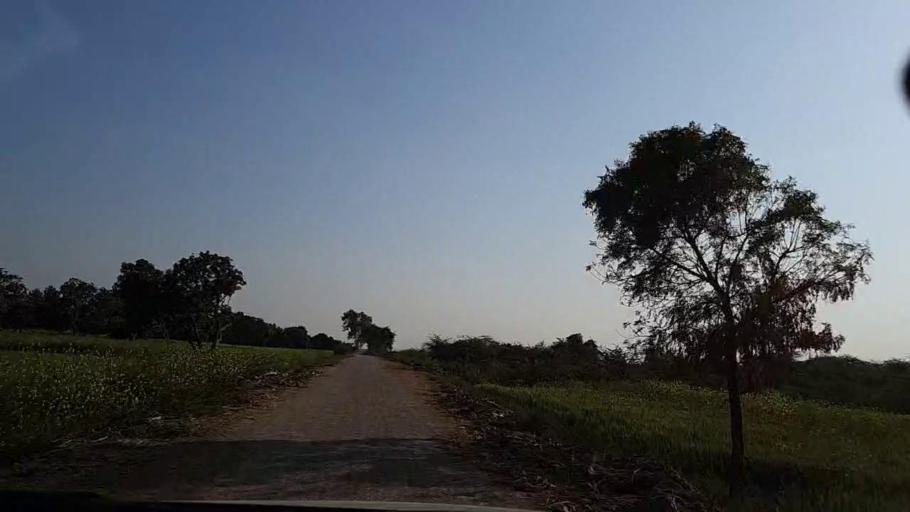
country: PK
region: Sindh
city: Mirwah Gorchani
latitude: 25.2317
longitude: 68.9731
